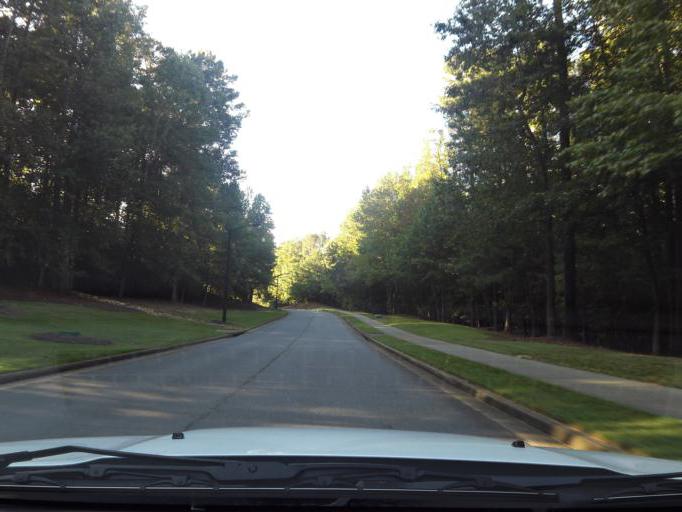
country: US
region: Georgia
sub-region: Cobb County
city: Kennesaw
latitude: 34.0507
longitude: -84.6288
